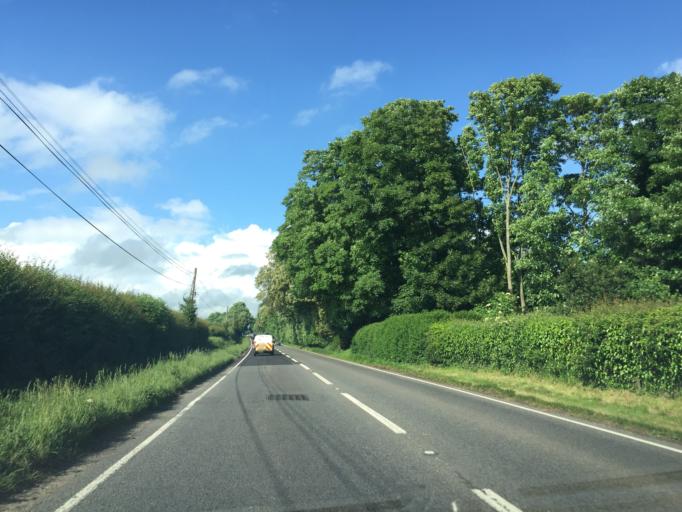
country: GB
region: England
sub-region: Dorset
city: Dorchester
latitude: 50.7225
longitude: -2.4117
